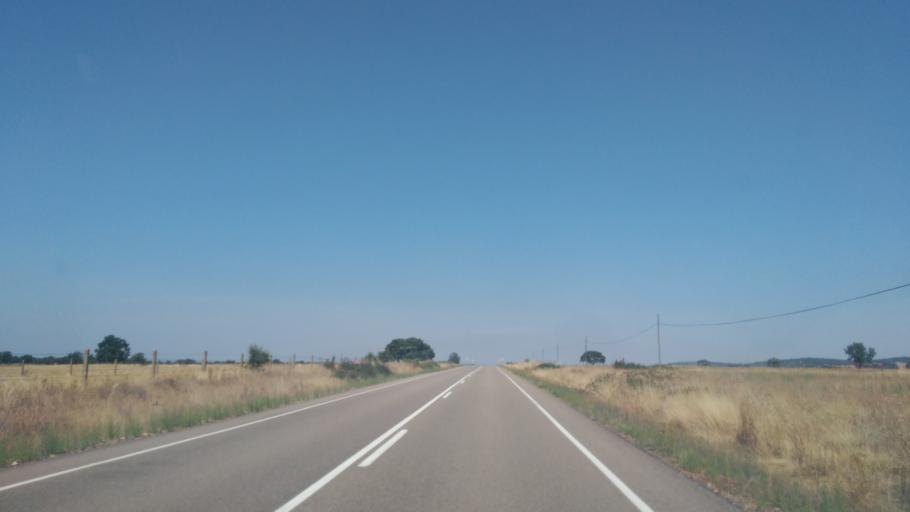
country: ES
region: Castille and Leon
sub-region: Provincia de Salamanca
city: Aldeanueva de la Sierra
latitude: 40.6221
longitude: -6.1039
